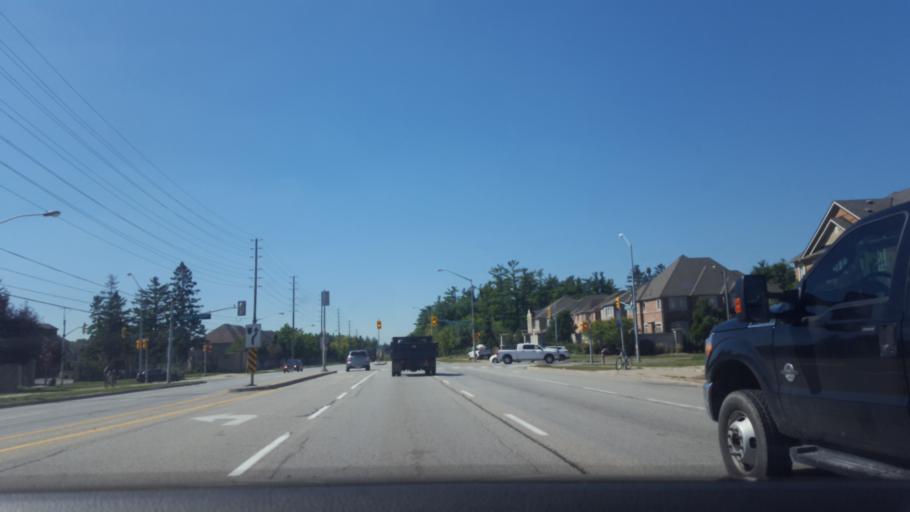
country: CA
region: Ontario
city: Vaughan
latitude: 43.8223
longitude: -79.5753
